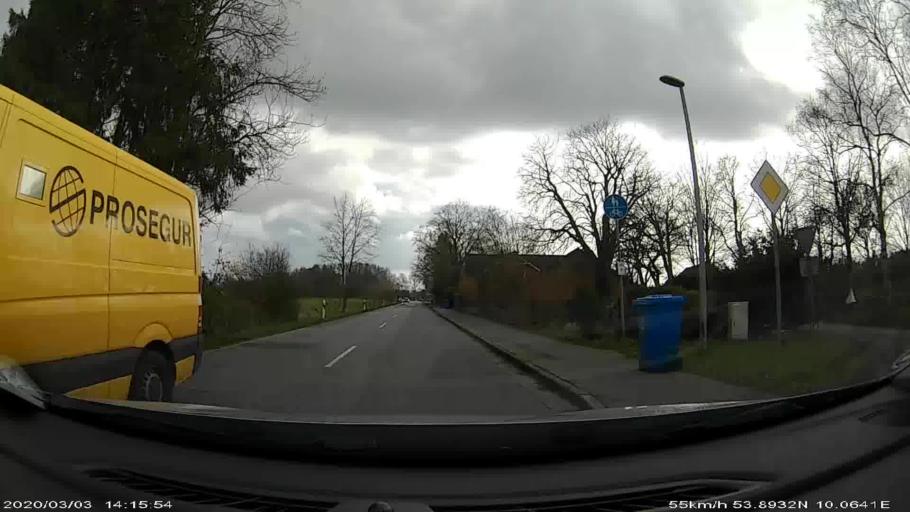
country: DE
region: Schleswig-Holstein
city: Hartenholm
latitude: 53.8927
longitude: 10.0643
